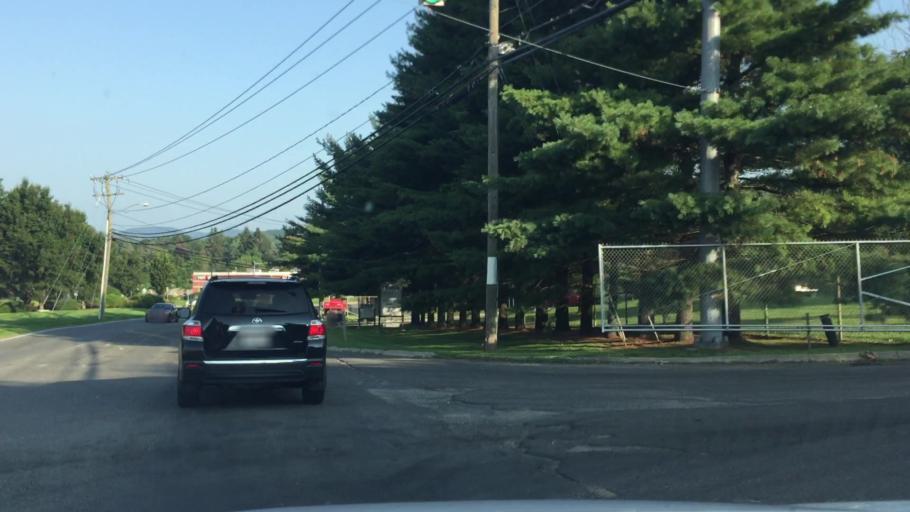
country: US
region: Massachusetts
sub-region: Berkshire County
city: Dalton
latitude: 42.4676
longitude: -73.1948
